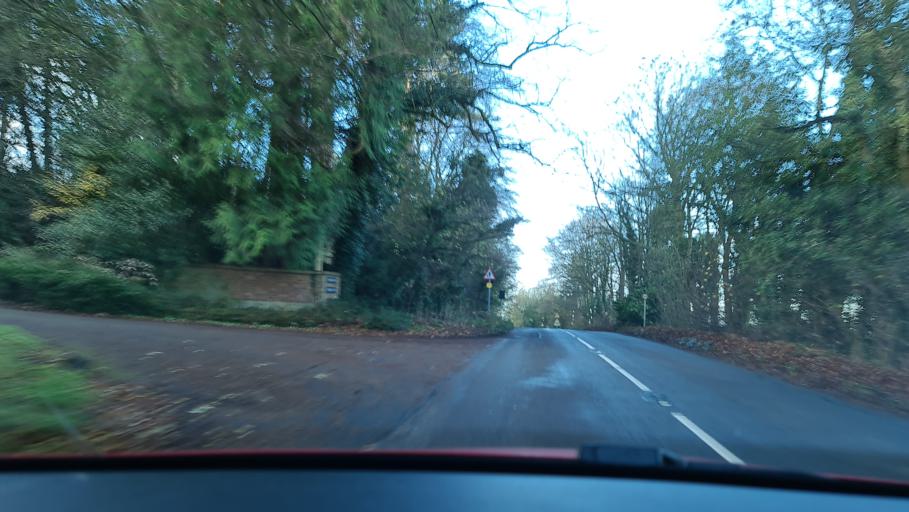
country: GB
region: England
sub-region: Buckinghamshire
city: Wendover
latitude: 51.7567
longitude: -0.7721
